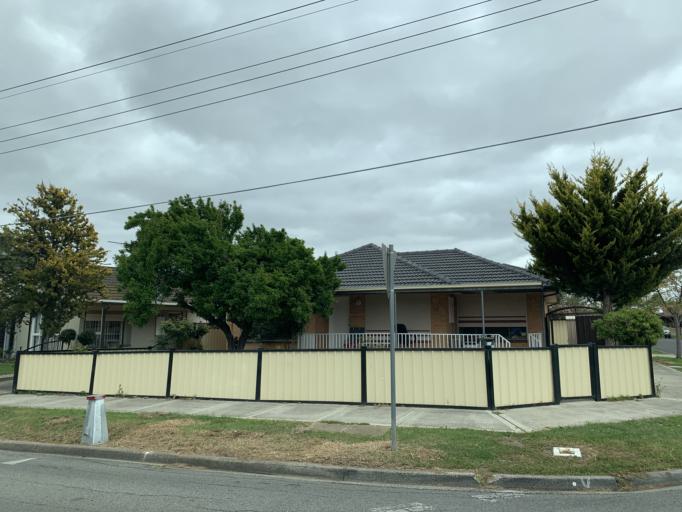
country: AU
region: Victoria
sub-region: Brimbank
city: Kealba
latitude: -37.7425
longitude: 144.8163
